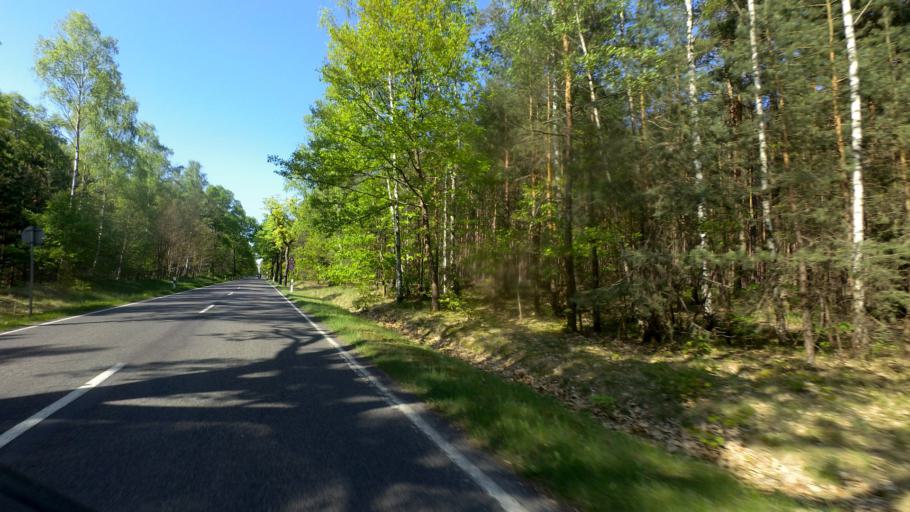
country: DE
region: Brandenburg
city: Gross Koris
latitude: 52.1938
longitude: 13.6966
